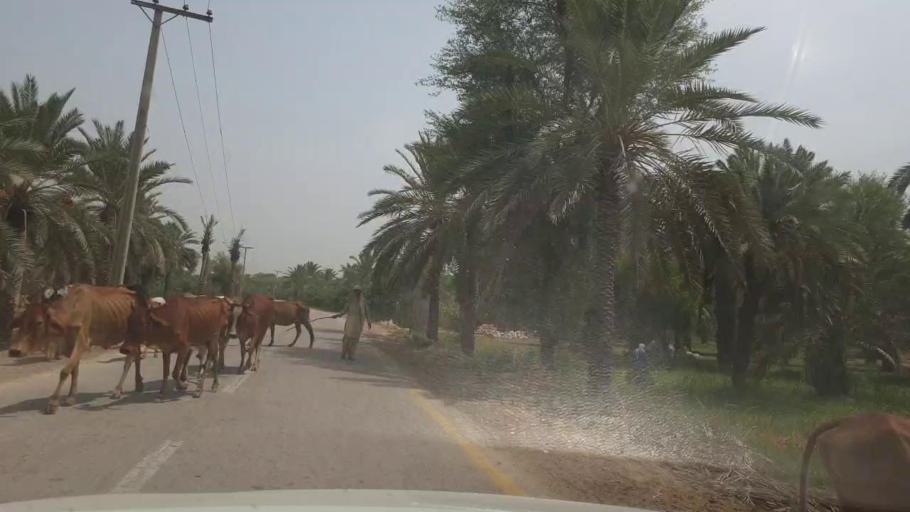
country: PK
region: Sindh
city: Kot Diji
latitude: 27.3660
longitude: 68.6434
